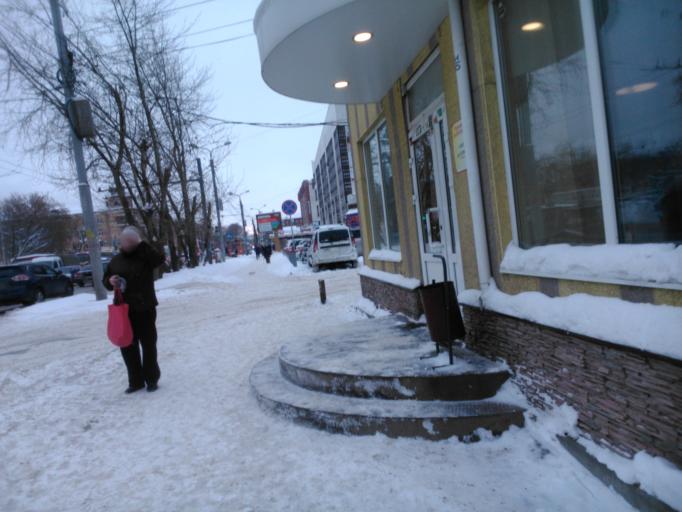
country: RU
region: Perm
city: Perm
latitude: 57.9915
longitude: 56.2483
